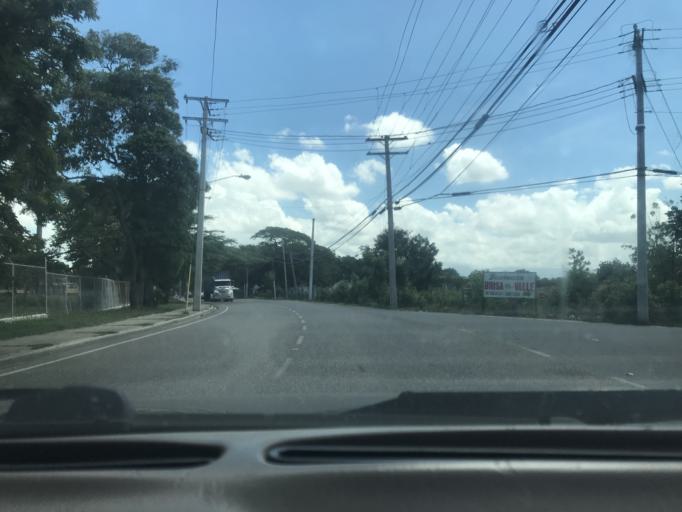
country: DO
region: Santiago
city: Santiago de los Caballeros
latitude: 19.4088
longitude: -70.7188
